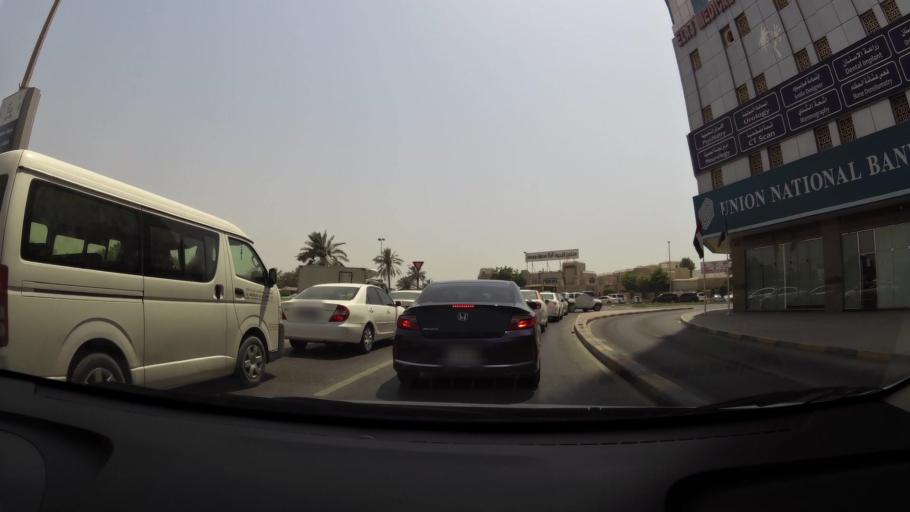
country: AE
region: Ajman
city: Ajman
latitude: 25.3941
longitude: 55.4277
